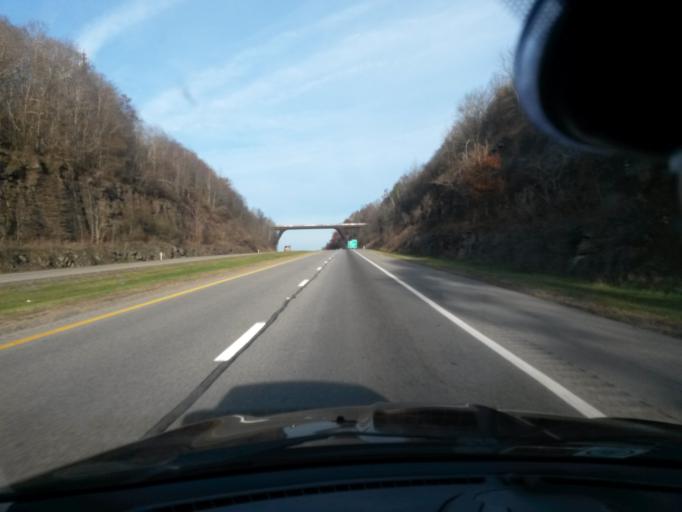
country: US
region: West Virginia
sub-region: Greenbrier County
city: Lewisburg
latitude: 37.9004
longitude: -80.5916
